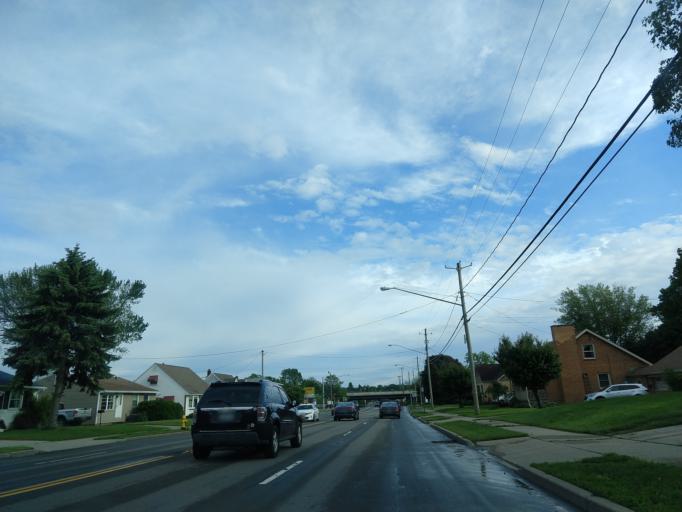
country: US
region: New York
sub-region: Erie County
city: Sloan
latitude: 42.8790
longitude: -78.7848
